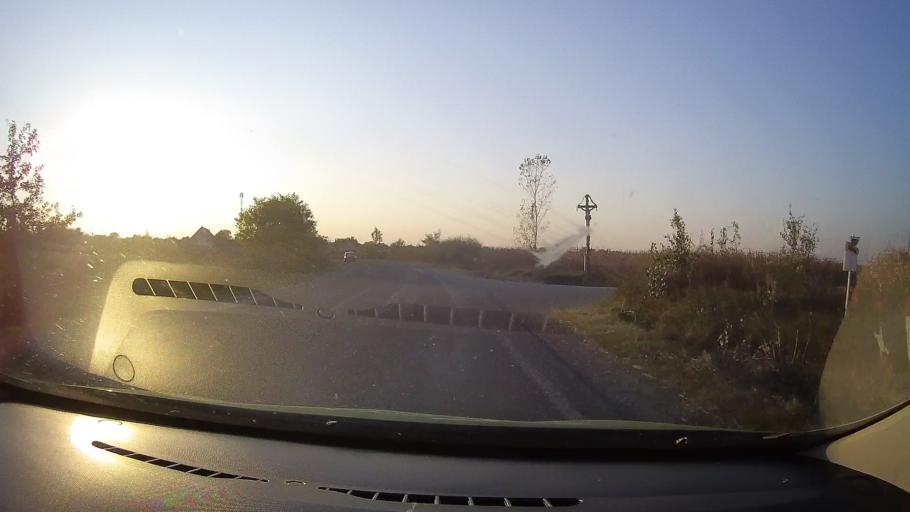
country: RO
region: Arad
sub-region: Comuna Bocsig
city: Bocsig
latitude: 46.4226
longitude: 21.9521
